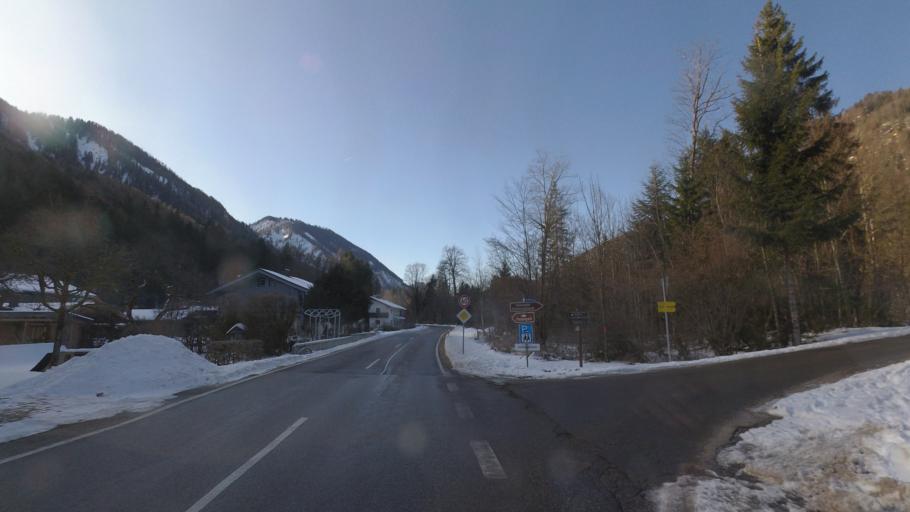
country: DE
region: Bavaria
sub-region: Upper Bavaria
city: Ruhpolding
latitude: 47.7415
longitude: 12.6150
